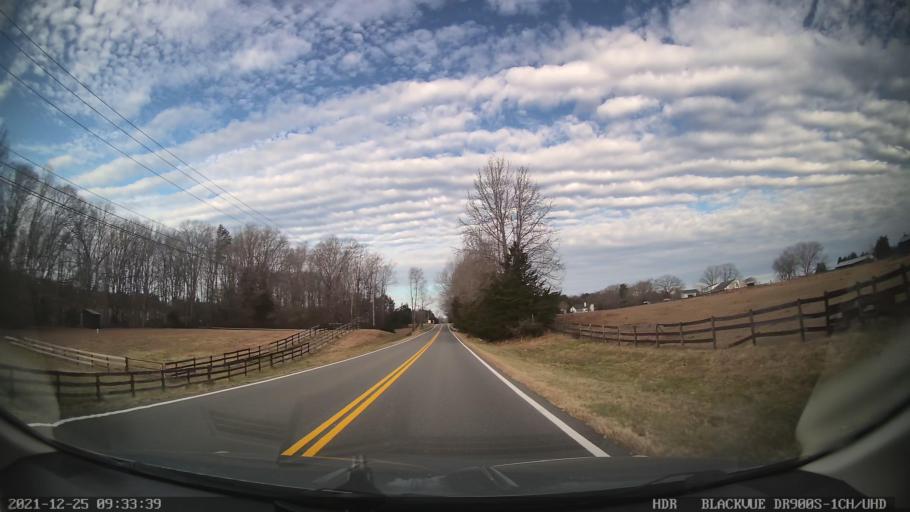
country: US
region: Virginia
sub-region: Goochland County
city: Goochland
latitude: 37.7424
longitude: -77.8474
